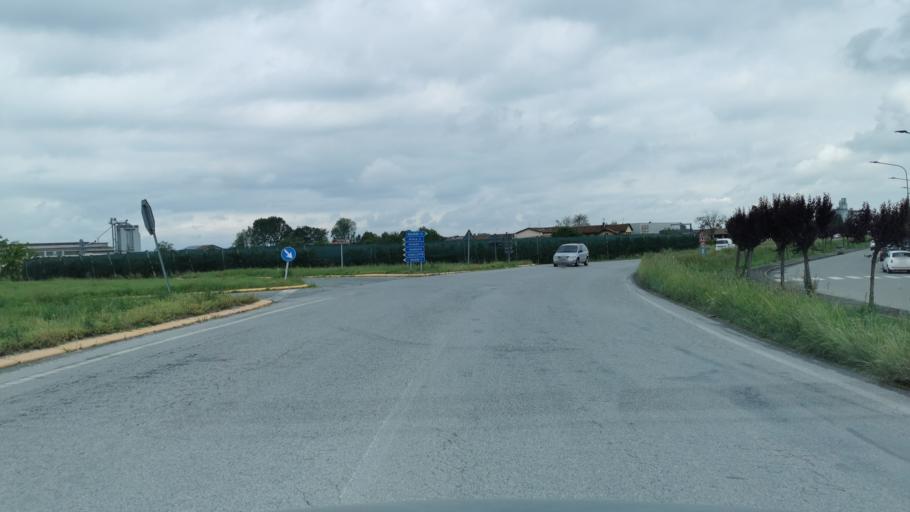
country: IT
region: Piedmont
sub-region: Provincia di Cuneo
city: Savigliano
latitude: 44.6409
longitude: 7.6464
